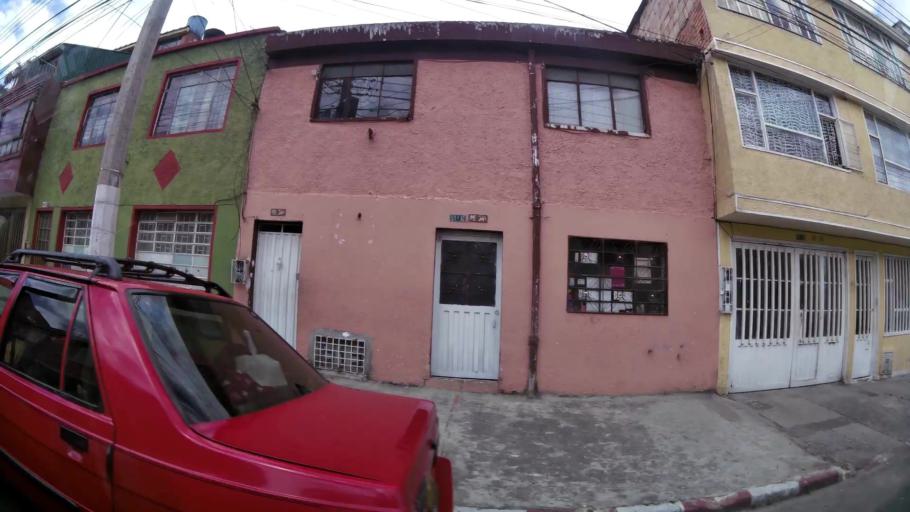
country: CO
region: Bogota D.C.
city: Bogota
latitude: 4.6030
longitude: -74.1250
